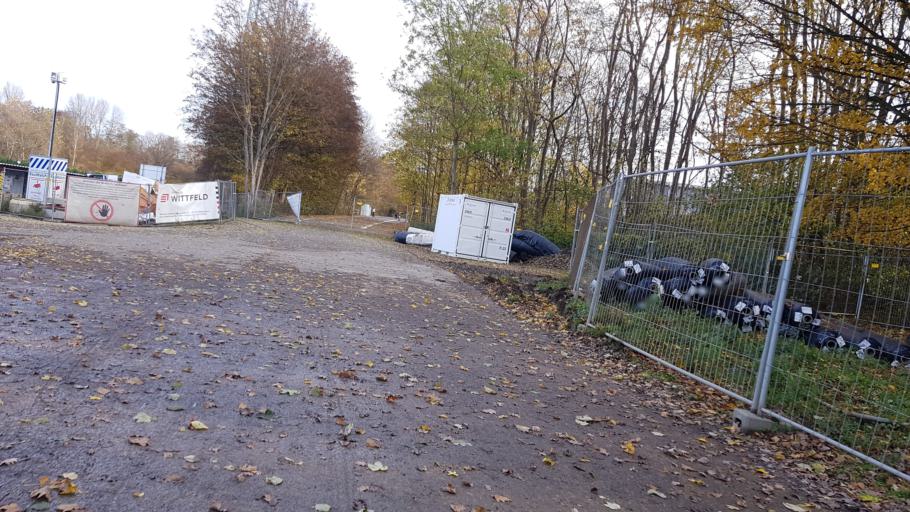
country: DE
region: North Rhine-Westphalia
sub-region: Regierungsbezirk Munster
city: Gelsenkirchen
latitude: 51.4876
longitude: 7.1179
